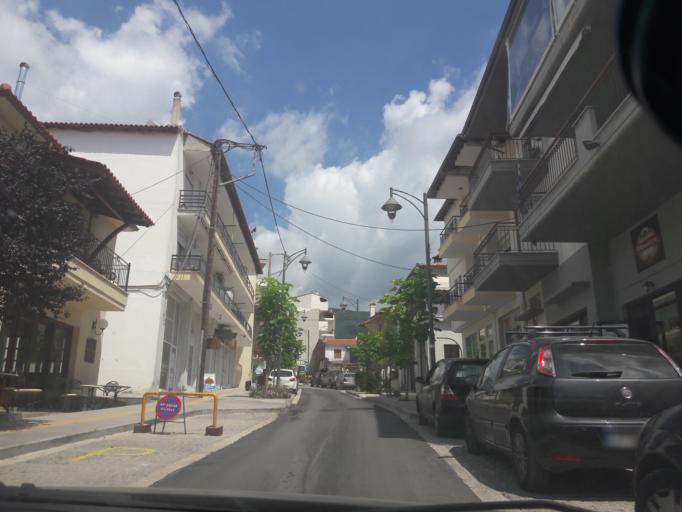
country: GR
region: Central Macedonia
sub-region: Nomos Chalkidikis
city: Polygyros
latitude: 40.3782
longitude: 23.4407
